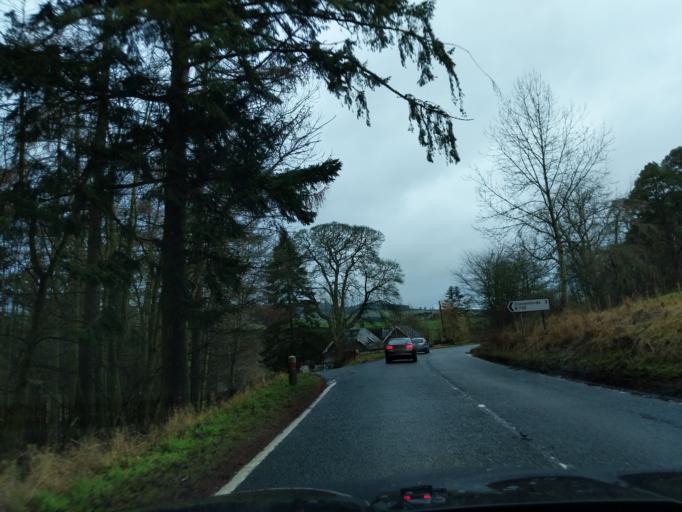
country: GB
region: Scotland
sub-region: The Scottish Borders
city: Galashiels
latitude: 55.6522
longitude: -2.8643
